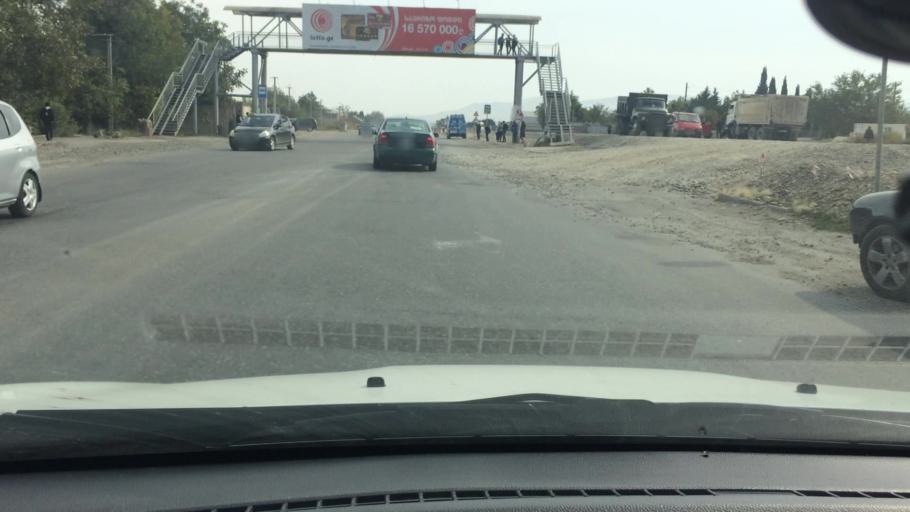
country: GE
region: T'bilisi
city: Tbilisi
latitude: 41.6396
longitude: 44.9150
